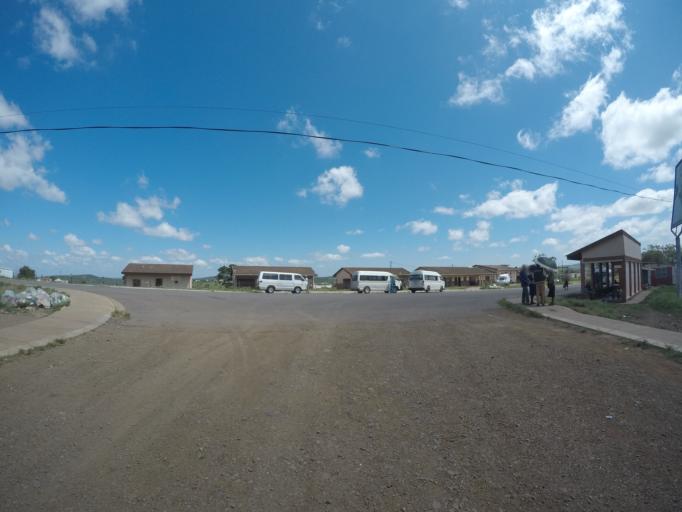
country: ZA
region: KwaZulu-Natal
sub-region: uThungulu District Municipality
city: Empangeni
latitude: -28.6052
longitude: 31.7448
